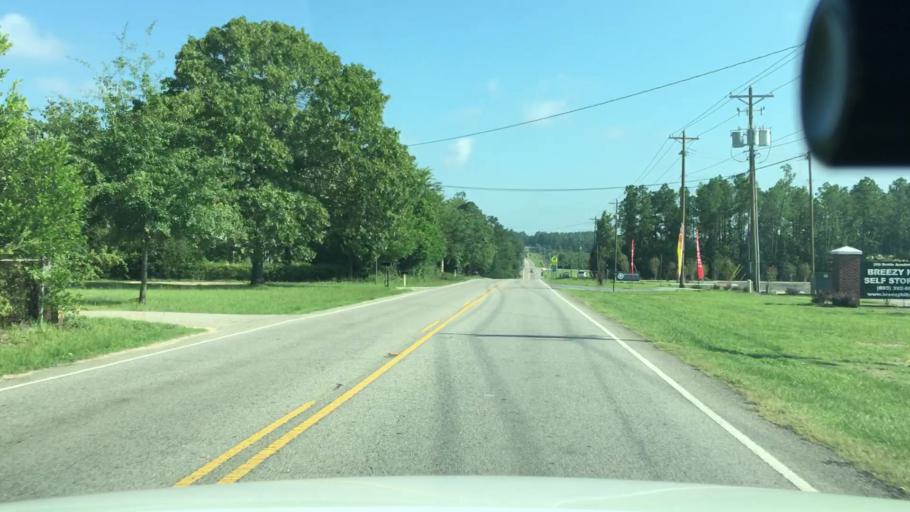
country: US
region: South Carolina
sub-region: Aiken County
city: Graniteville
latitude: 33.5789
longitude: -81.8359
